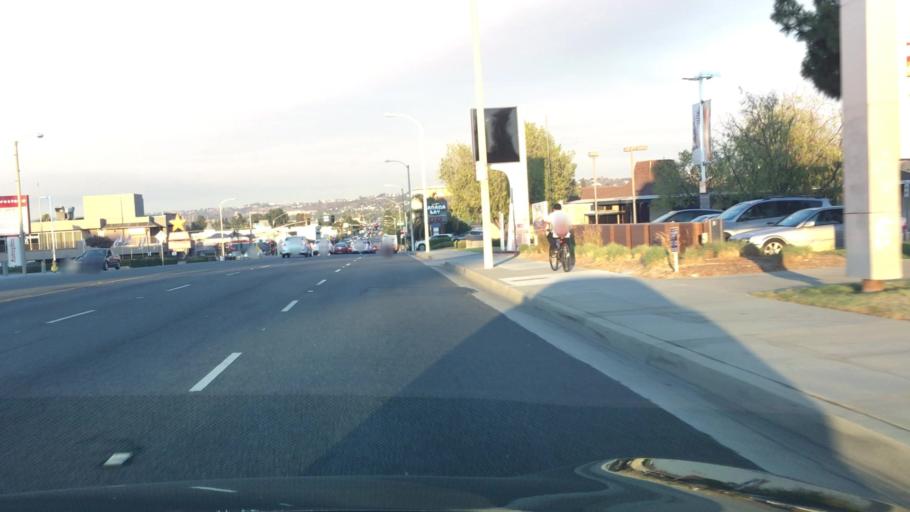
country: US
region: California
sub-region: Los Angeles County
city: Rowland Heights
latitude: 33.9885
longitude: -117.9078
